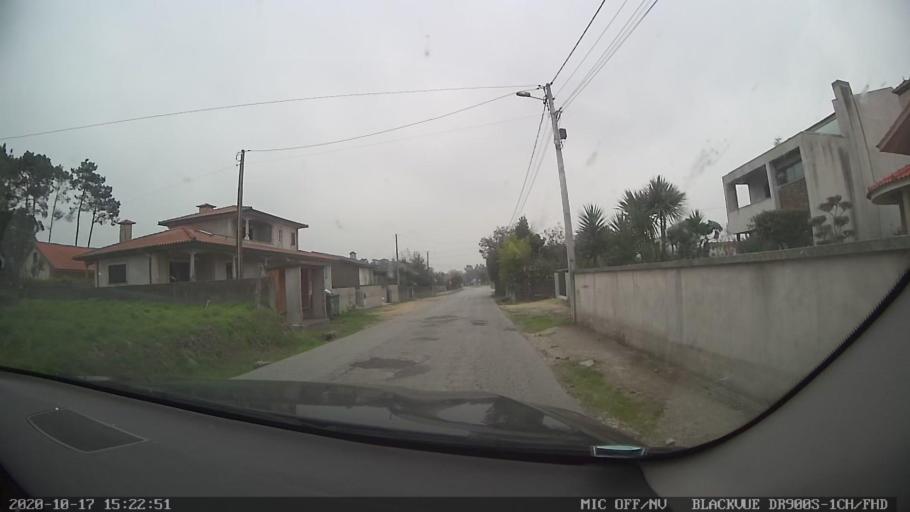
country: PT
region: Braga
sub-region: Esposende
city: Esposende
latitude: 41.5315
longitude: -8.7373
